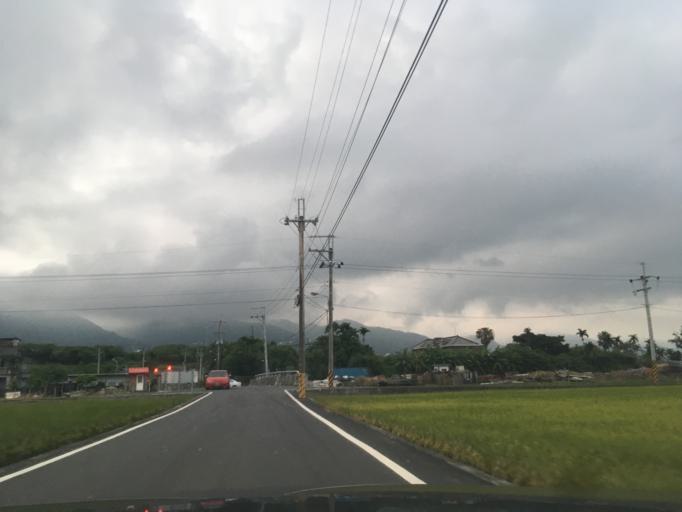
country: TW
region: Taiwan
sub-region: Yilan
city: Yilan
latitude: 24.8209
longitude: 121.7864
